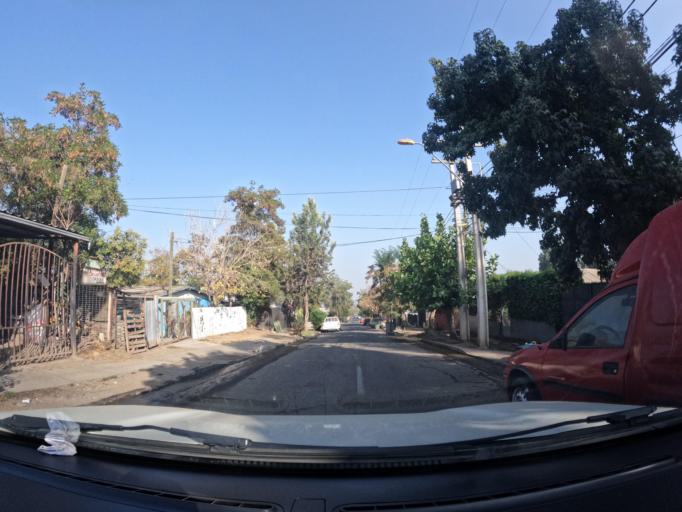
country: CL
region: Santiago Metropolitan
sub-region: Provincia de Santiago
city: Villa Presidente Frei, Nunoa, Santiago, Chile
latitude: -33.4691
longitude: -70.5265
